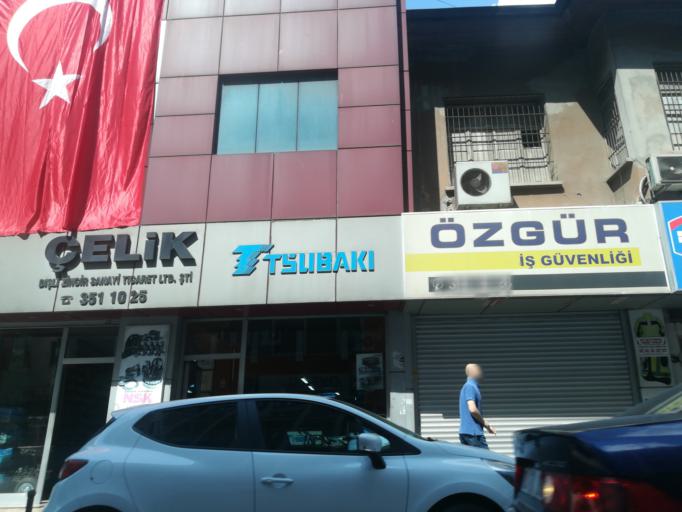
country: TR
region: Adana
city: Adana
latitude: 36.9854
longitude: 35.3274
